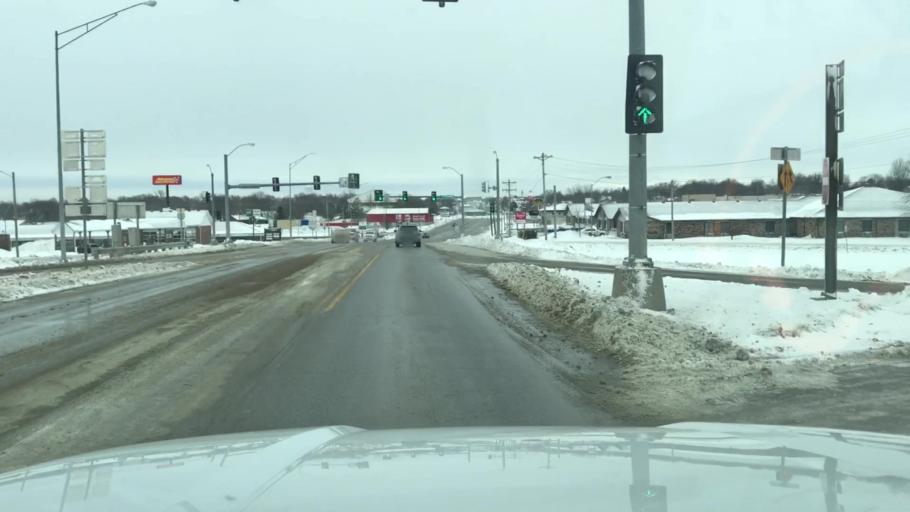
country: US
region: Missouri
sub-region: Clinton County
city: Cameron
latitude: 39.7538
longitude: -94.2343
